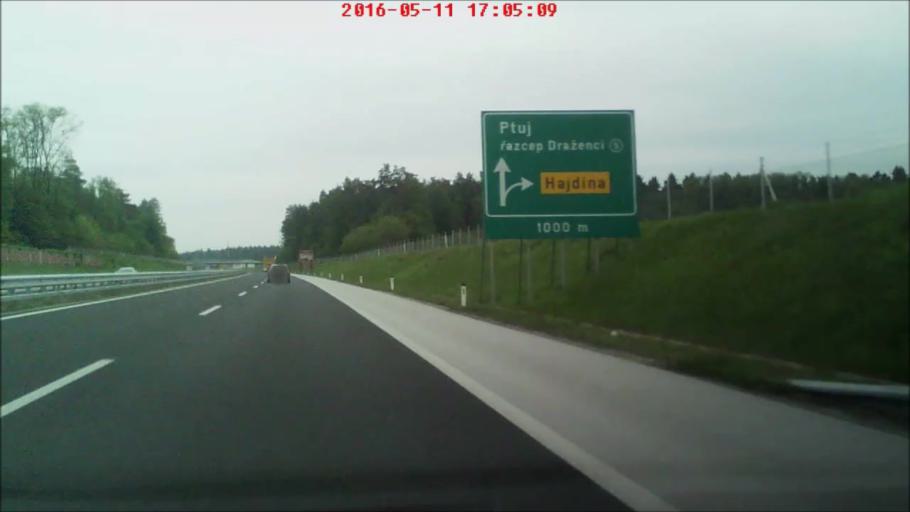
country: SI
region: Kidricevo
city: Kidricevo
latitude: 46.4216
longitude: 15.8010
